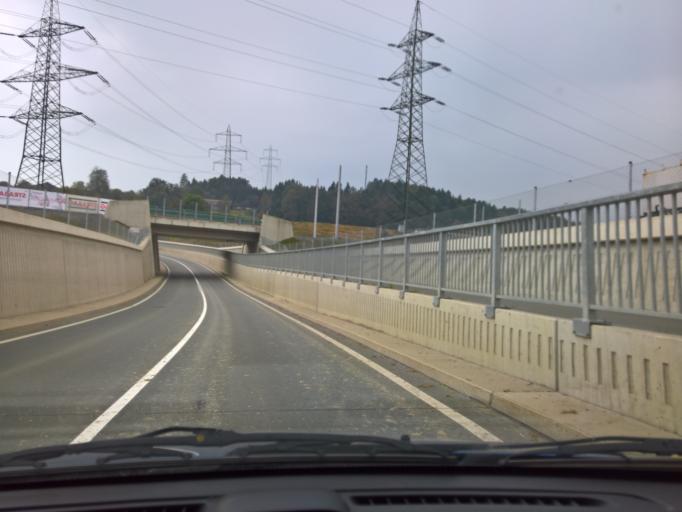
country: AT
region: Styria
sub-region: Politischer Bezirk Deutschlandsberg
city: Gross Sankt Florian
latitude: 46.8143
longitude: 15.3149
